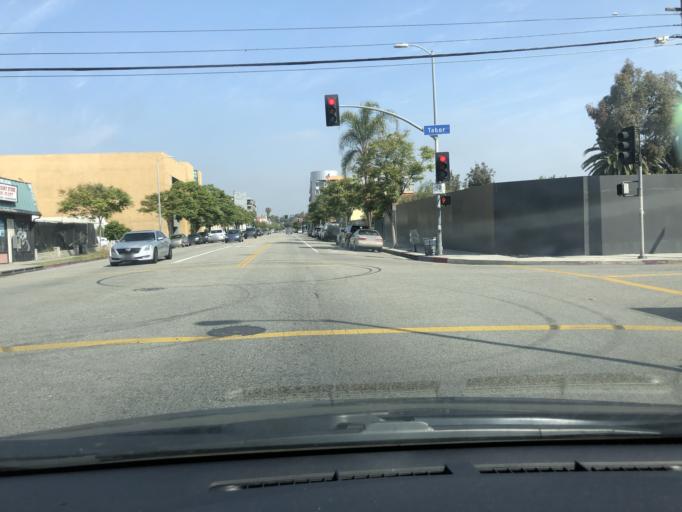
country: US
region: California
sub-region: Los Angeles County
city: Culver City
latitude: 34.0249
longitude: -118.4073
